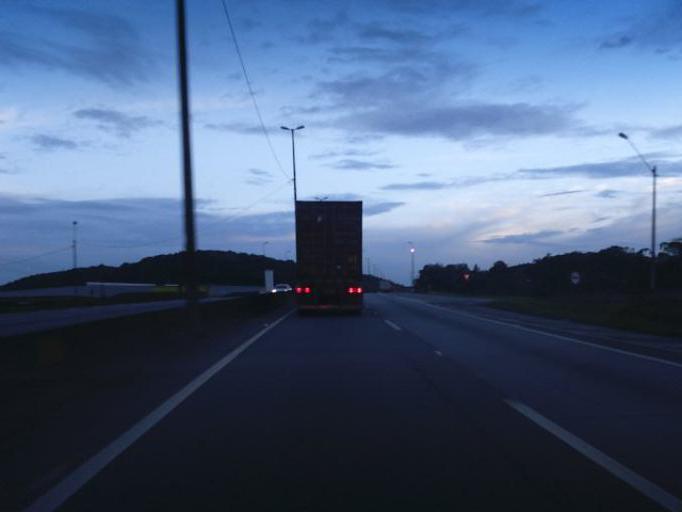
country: BR
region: Santa Catarina
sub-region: Joinville
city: Joinville
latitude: -26.2556
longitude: -48.9051
